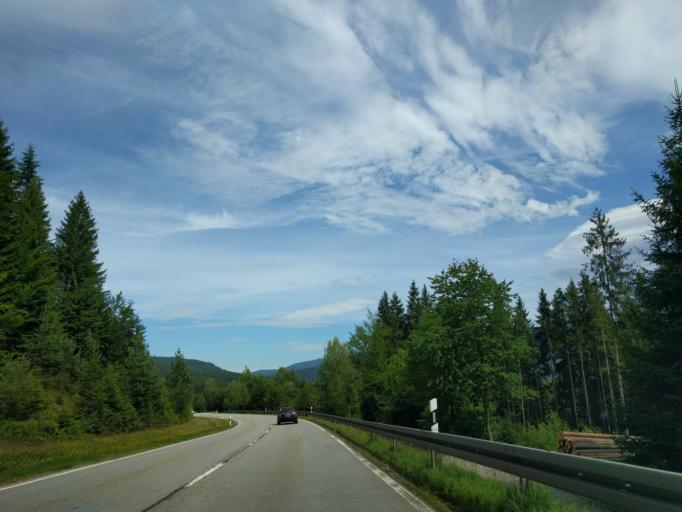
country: DE
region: Bavaria
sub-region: Lower Bavaria
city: Langdorf
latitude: 49.0203
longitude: 13.1382
